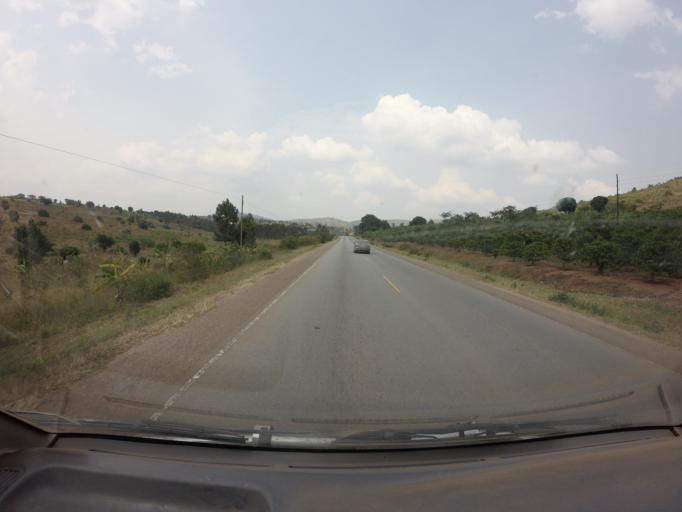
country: UG
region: Central Region
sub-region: Lyantonde District
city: Lyantonde
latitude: -0.3790
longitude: 31.2428
